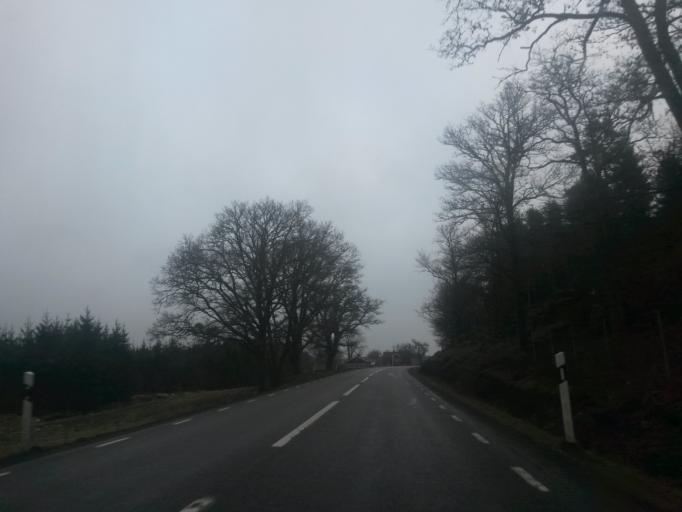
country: SE
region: Vaestra Goetaland
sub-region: Alingsas Kommun
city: Sollebrunn
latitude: 58.1548
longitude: 12.4208
